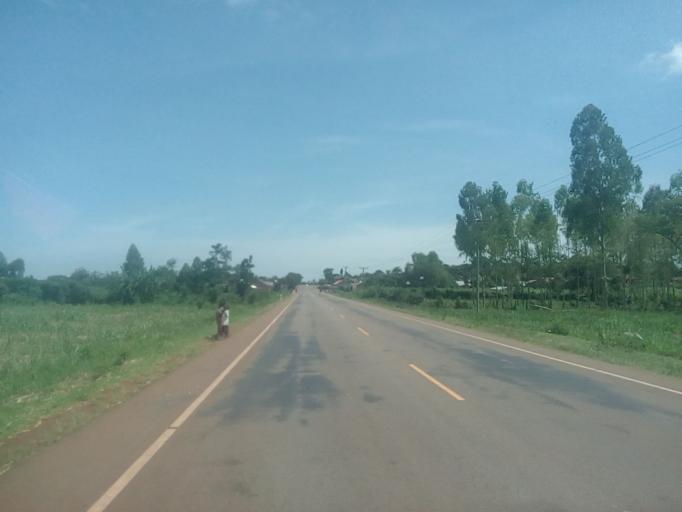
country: UG
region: Eastern Region
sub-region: Kamuli District
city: Kamuli
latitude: 0.8868
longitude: 33.1220
